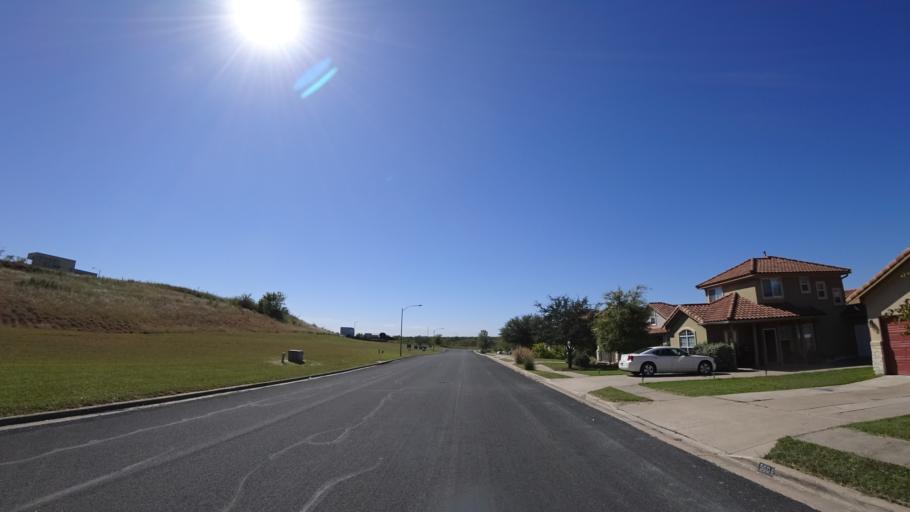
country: US
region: Texas
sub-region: Travis County
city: Hornsby Bend
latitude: 30.2872
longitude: -97.6455
